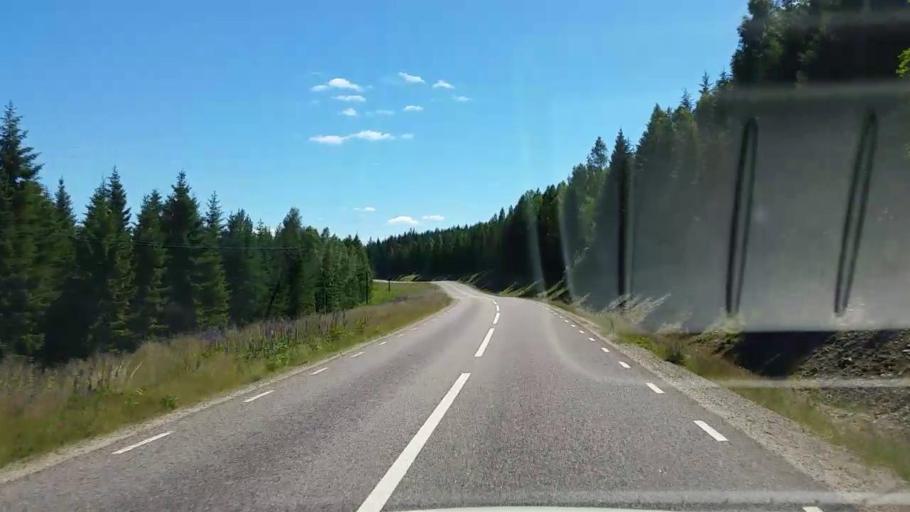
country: SE
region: Gaevleborg
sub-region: Ovanakers Kommun
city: Edsbyn
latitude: 61.5781
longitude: 15.6613
